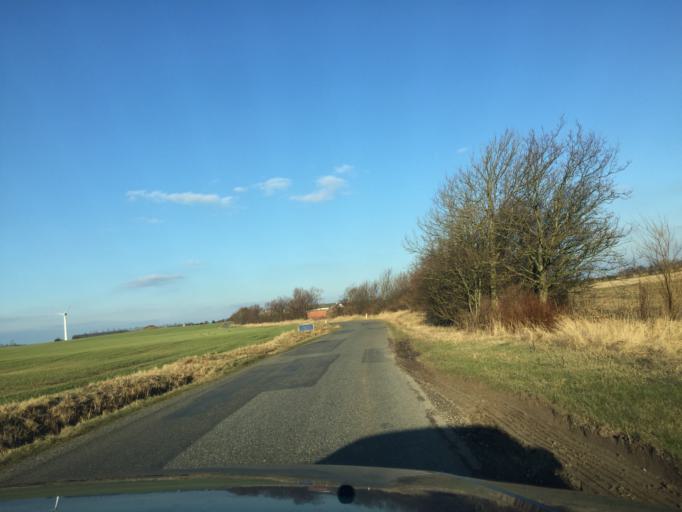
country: DK
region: Central Jutland
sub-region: Holstebro Kommune
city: Vinderup
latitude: 56.6070
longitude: 8.8102
